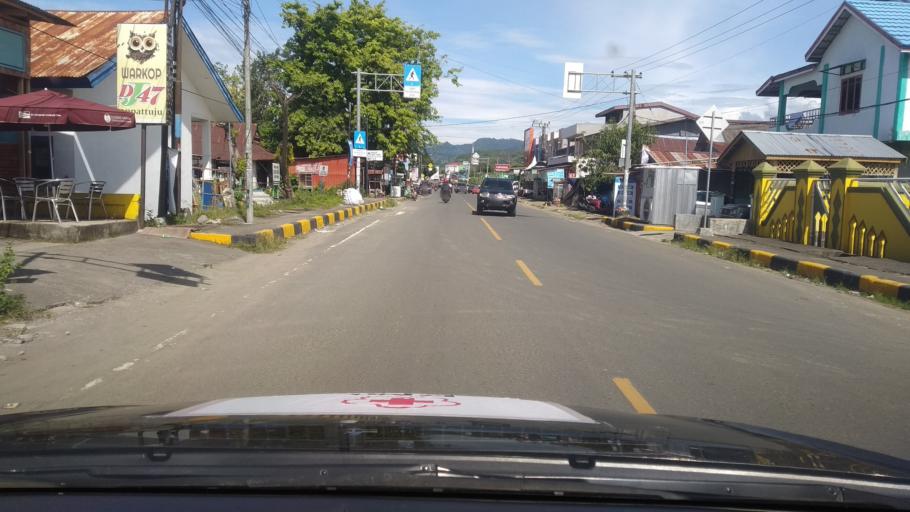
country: ID
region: Sulawesi Barat
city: Mamuju
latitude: -2.6825
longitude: 118.8718
